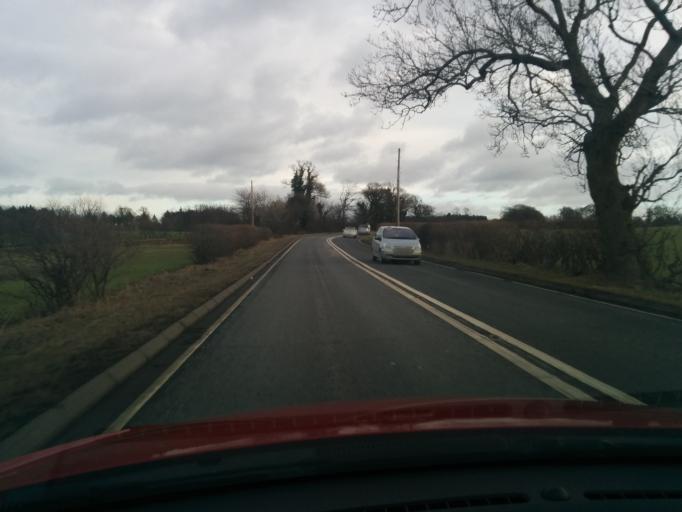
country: GB
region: Scotland
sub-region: Fife
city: Limekilns
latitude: 55.9832
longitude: -3.5061
